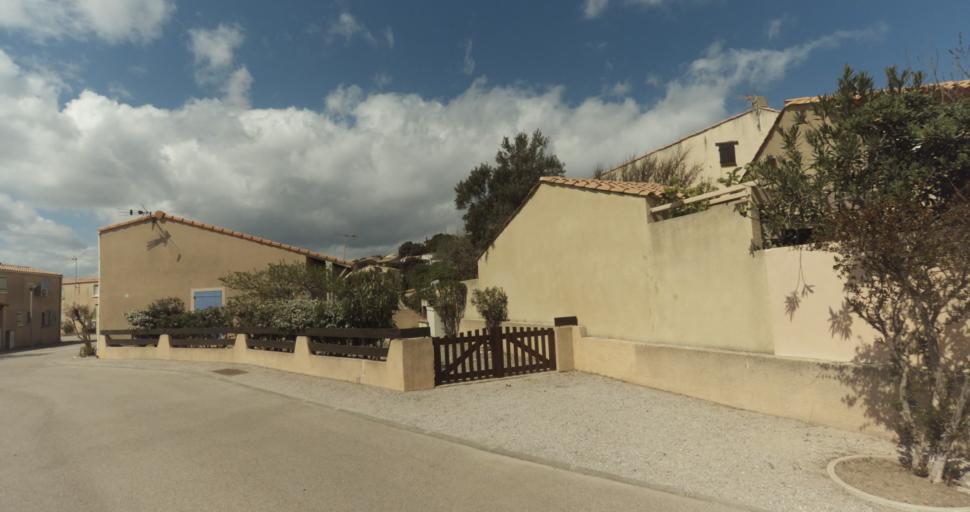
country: FR
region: Languedoc-Roussillon
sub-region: Departement de l'Aude
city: Leucate
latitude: 42.9034
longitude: 3.0540
